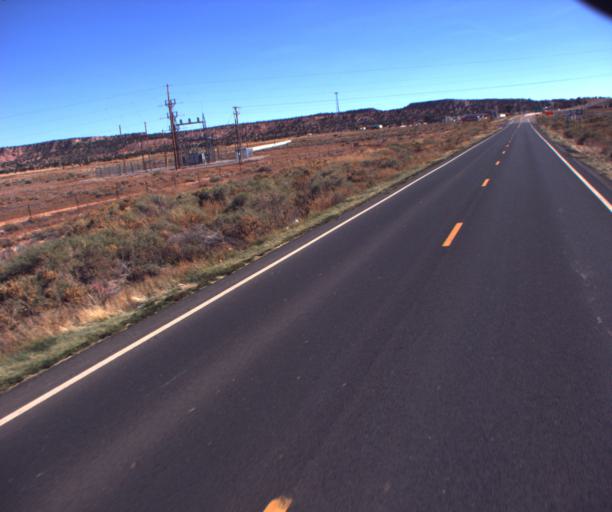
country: US
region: Arizona
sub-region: Apache County
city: Ganado
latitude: 35.7584
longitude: -109.6317
